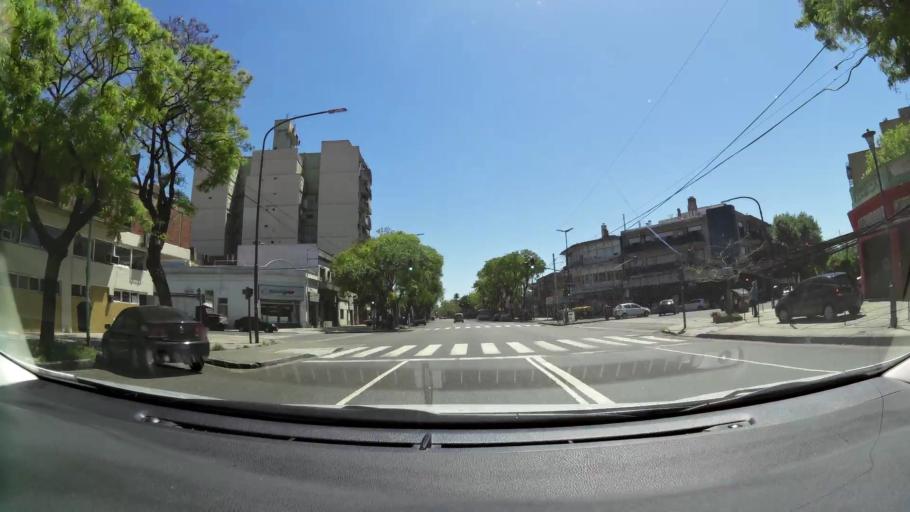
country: AR
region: Buenos Aires
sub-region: Partido de Avellaneda
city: Avellaneda
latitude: -34.6459
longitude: -58.4147
